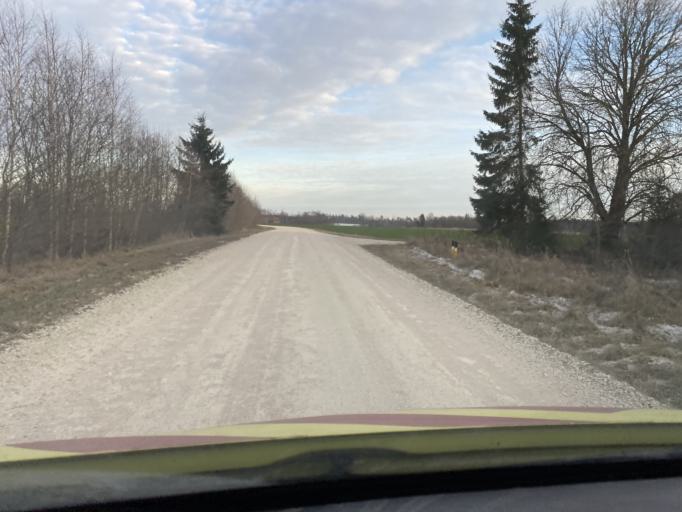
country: EE
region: Jogevamaa
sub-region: Poltsamaa linn
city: Poltsamaa
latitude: 58.5829
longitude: 26.1751
